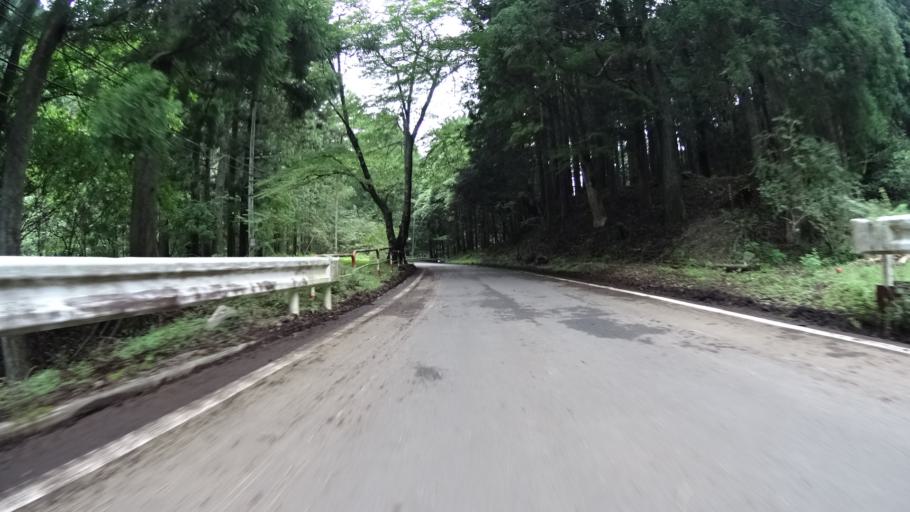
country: JP
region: Kanagawa
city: Hadano
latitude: 35.4560
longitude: 139.2135
